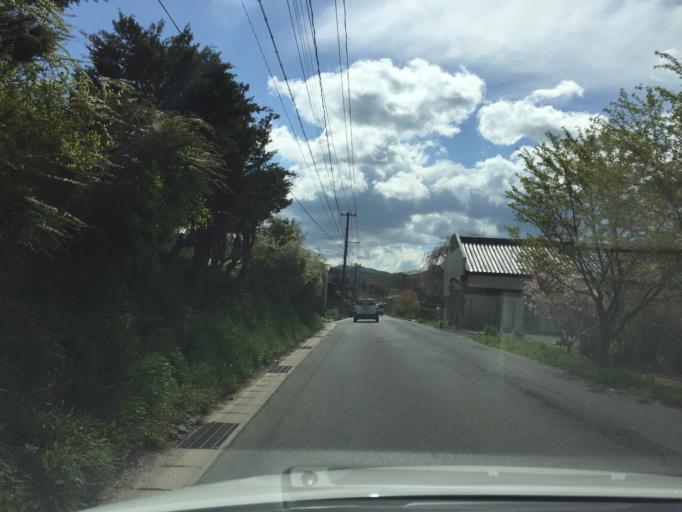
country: JP
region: Fukushima
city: Funehikimachi-funehiki
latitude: 37.6074
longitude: 140.6671
